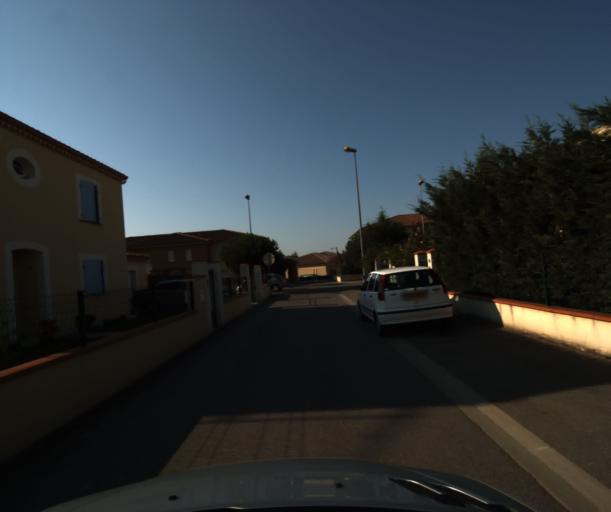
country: FR
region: Midi-Pyrenees
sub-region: Departement de la Haute-Garonne
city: Roquettes
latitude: 43.4785
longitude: 1.3877
